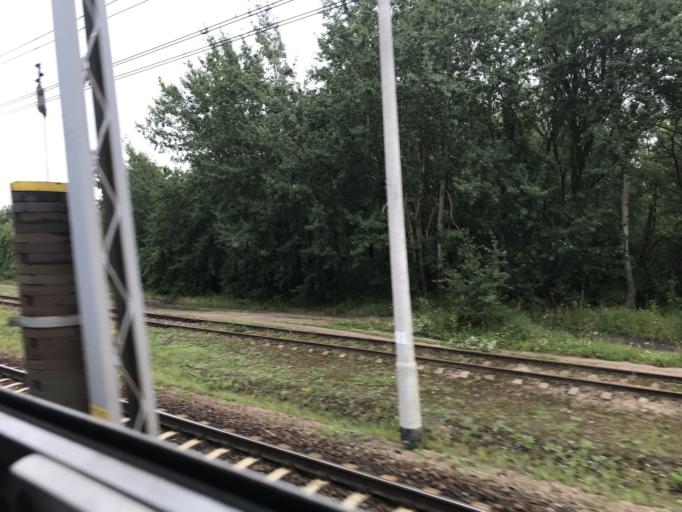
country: PL
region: Pomeranian Voivodeship
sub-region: Powiat gdanski
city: Pruszcz Gdanski
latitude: 54.2479
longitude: 18.6472
